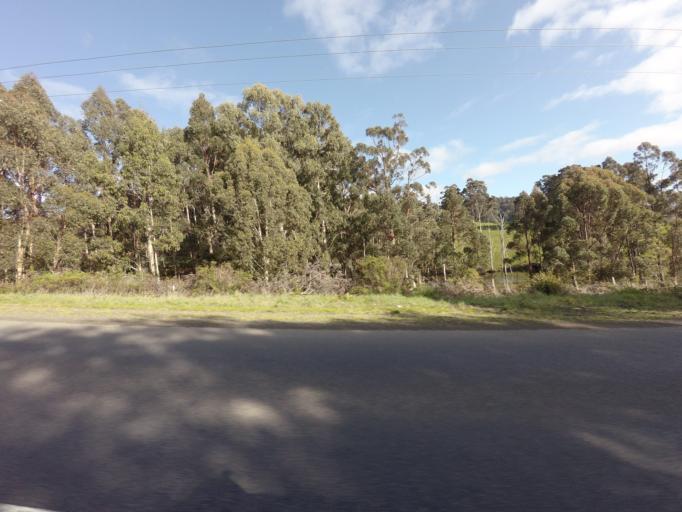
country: AU
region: Tasmania
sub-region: Huon Valley
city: Geeveston
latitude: -43.1941
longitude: 146.9573
